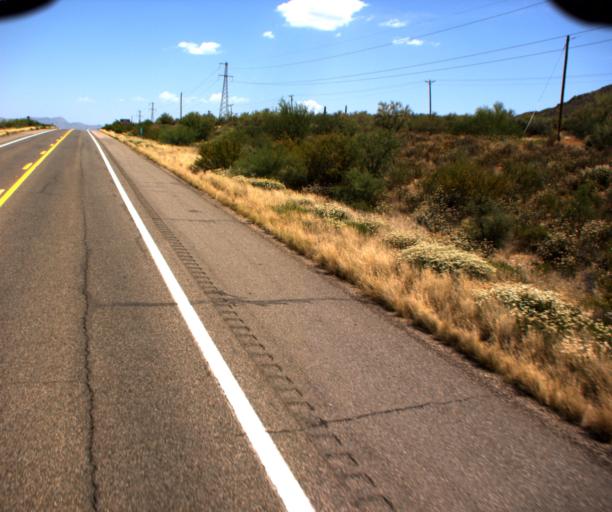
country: US
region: Arizona
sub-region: Gila County
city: Tonto Basin
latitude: 33.6563
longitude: -111.1089
